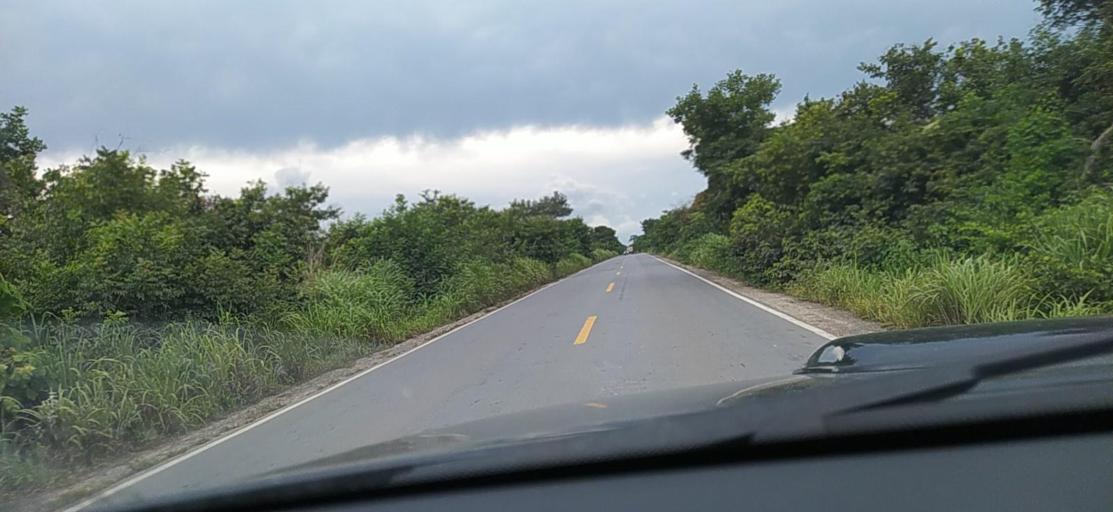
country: BR
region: Minas Gerais
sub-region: Francisco Sa
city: Francisco Sa
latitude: -16.2501
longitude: -43.6313
